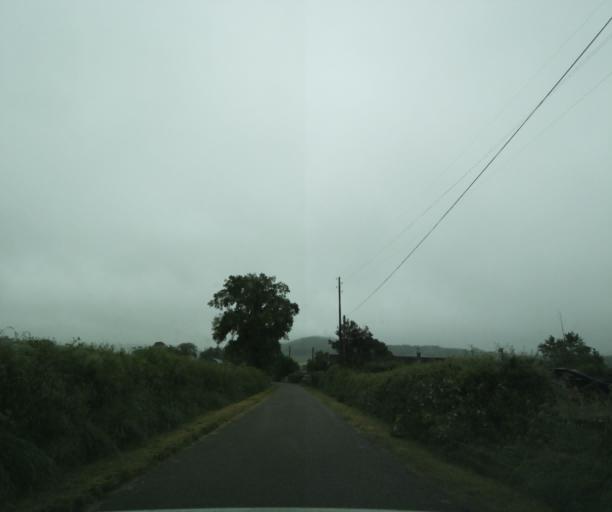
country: FR
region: Bourgogne
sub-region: Departement de Saone-et-Loire
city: Charolles
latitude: 46.4051
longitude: 4.3737
